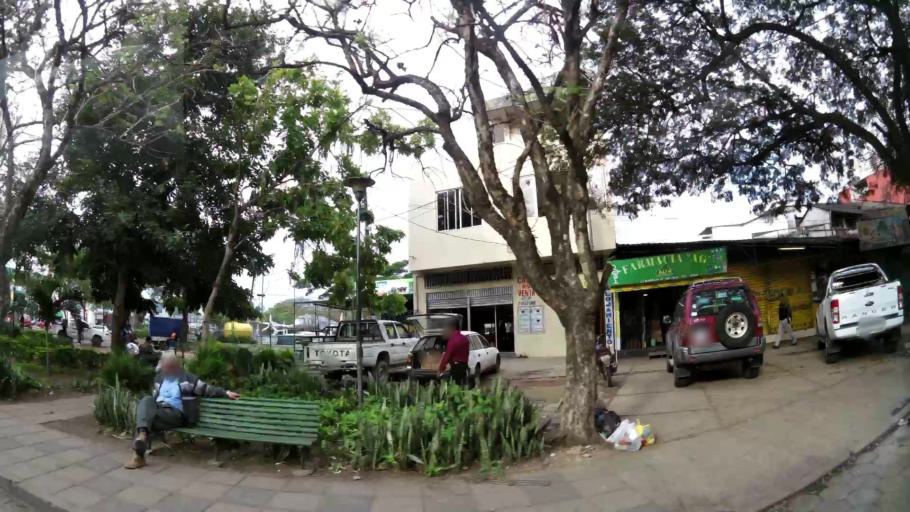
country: BO
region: Santa Cruz
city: Santa Cruz de la Sierra
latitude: -17.7761
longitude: -63.1748
